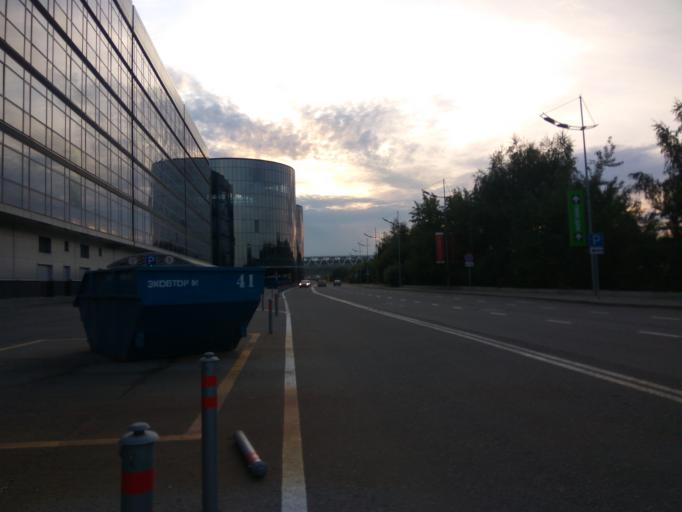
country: RU
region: Moscow
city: Strogino
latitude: 55.8288
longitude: 37.3902
